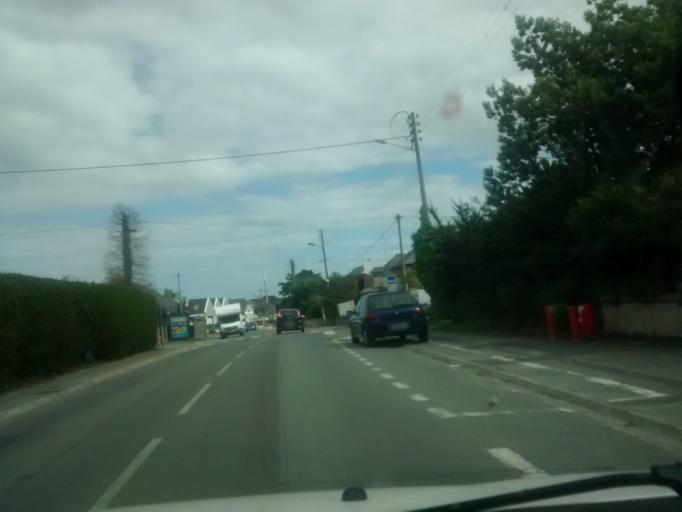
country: FR
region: Brittany
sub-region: Departement d'Ille-et-Vilaine
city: Dinard
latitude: 48.6324
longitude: -2.0841
